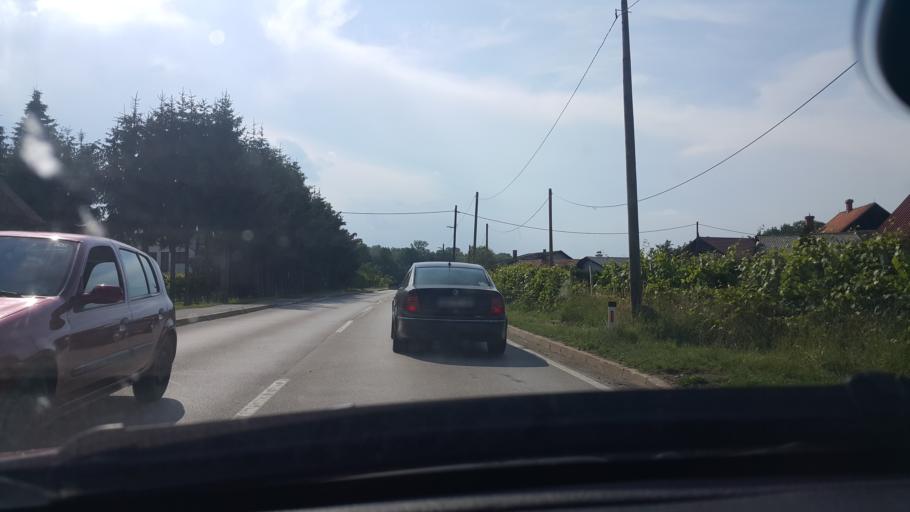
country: SI
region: Duplek
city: Zgornji Duplek
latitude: 46.5075
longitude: 15.7284
